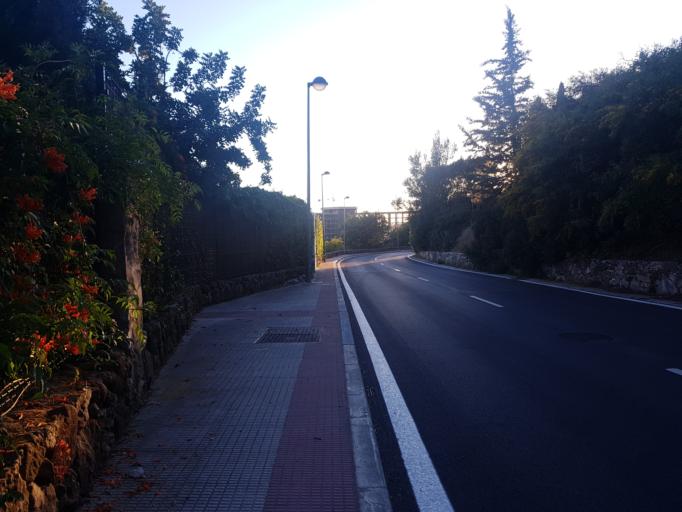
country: ES
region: Andalusia
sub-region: Provincia de Malaga
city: Marbella
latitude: 36.5276
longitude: -4.8883
